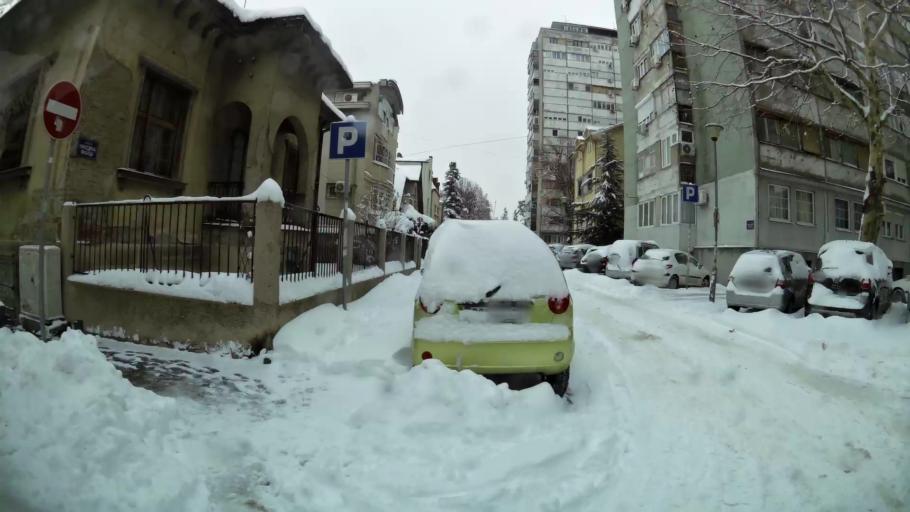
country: RS
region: Central Serbia
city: Belgrade
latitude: 44.8102
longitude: 20.4837
